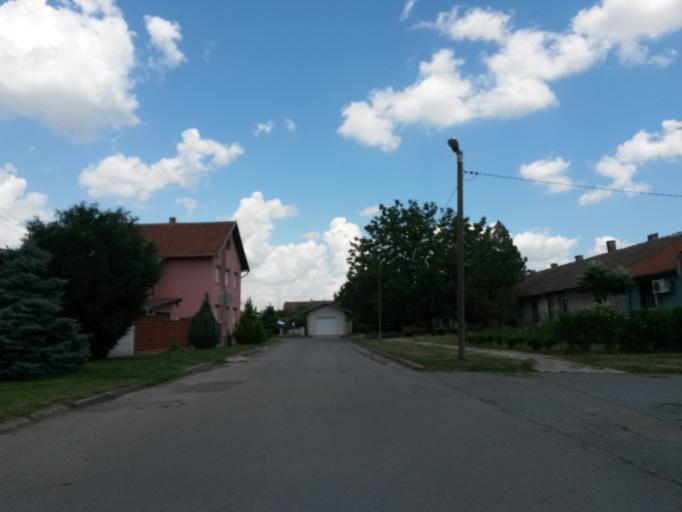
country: HR
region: Osjecko-Baranjska
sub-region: Grad Osijek
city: Osijek
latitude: 45.5480
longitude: 18.7195
